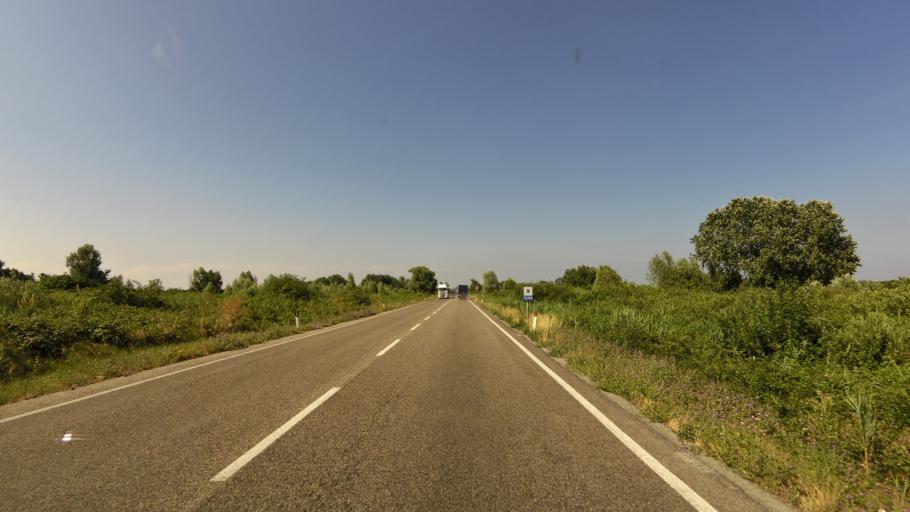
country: IT
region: Emilia-Romagna
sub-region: Provincia di Ravenna
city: Marina Romea
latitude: 44.5346
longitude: 12.2320
